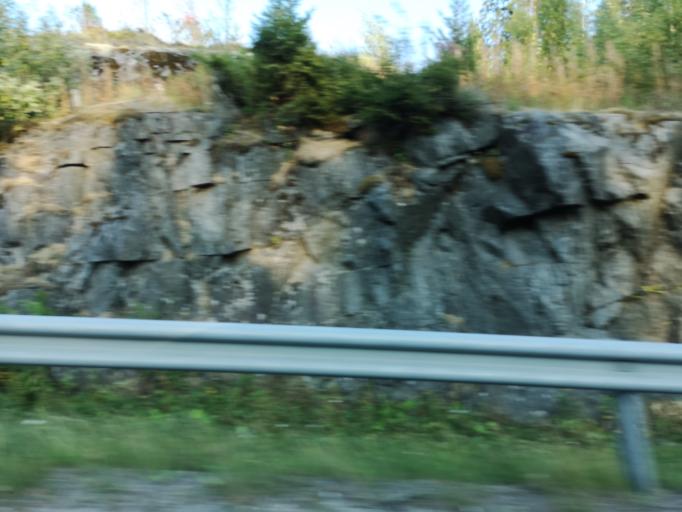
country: FI
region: Paijanne Tavastia
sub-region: Lahti
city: Heinola
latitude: 61.3377
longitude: 26.0417
